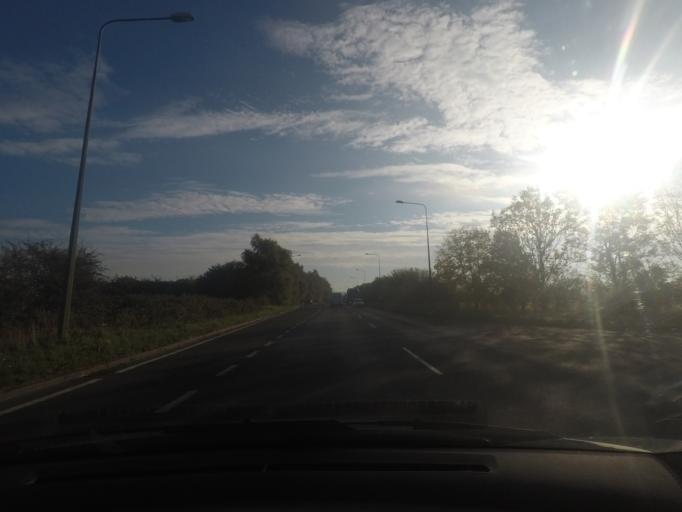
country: GB
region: England
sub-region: East Riding of Yorkshire
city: Market Weighton
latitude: 53.8579
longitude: -0.6731
